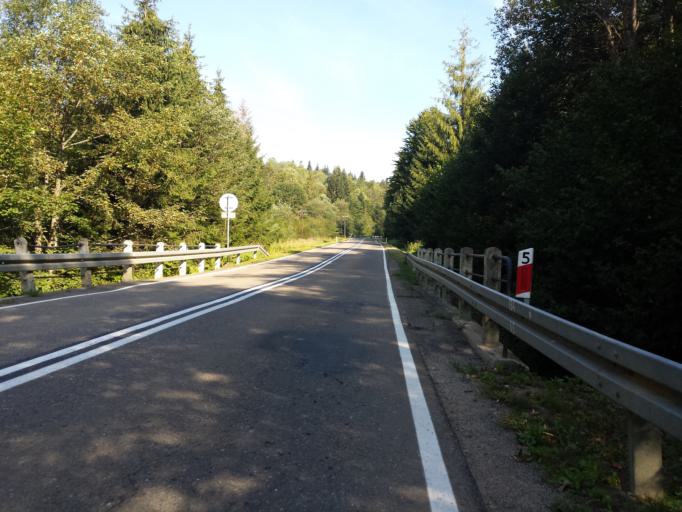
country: PL
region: Subcarpathian Voivodeship
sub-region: Powiat leski
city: Cisna
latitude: 49.2262
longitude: 22.3052
